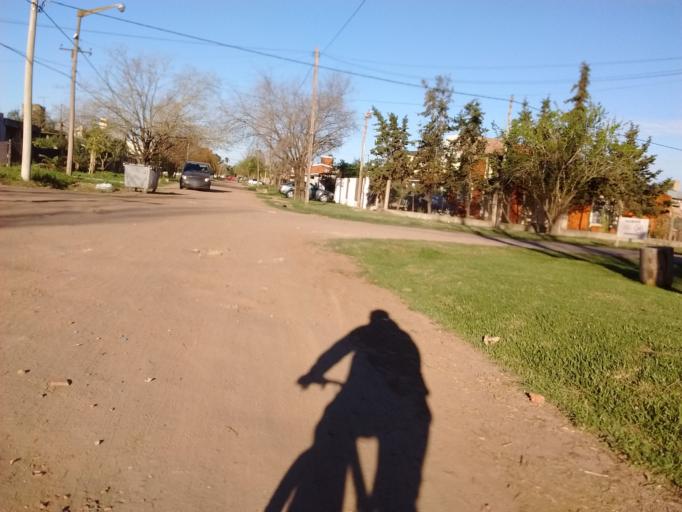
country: AR
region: Santa Fe
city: Funes
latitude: -32.9242
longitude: -60.7955
